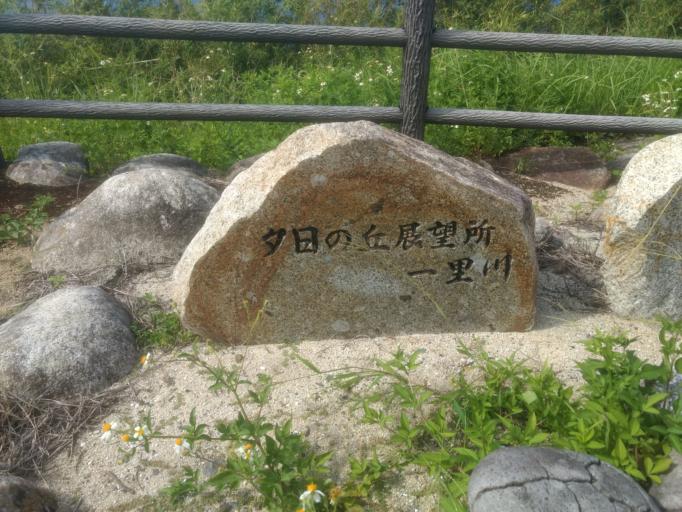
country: JP
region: Kagoshima
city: Nishinoomote
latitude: 30.4287
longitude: 130.4487
